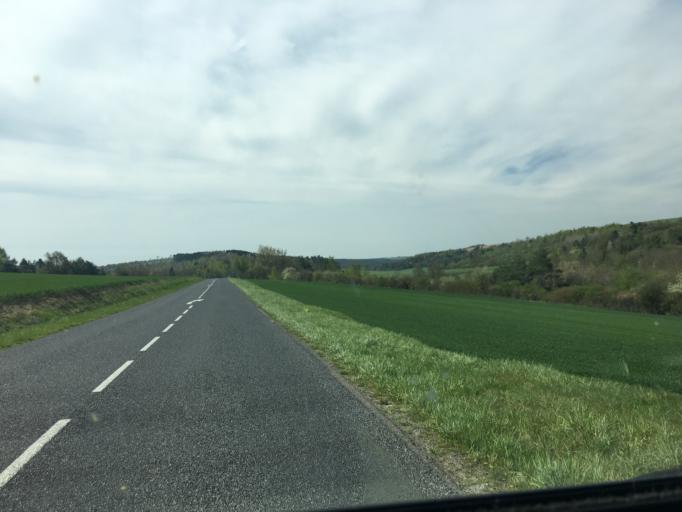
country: FR
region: Lorraine
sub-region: Departement de la Meuse
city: Saint-Mihiel
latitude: 48.8516
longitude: 5.5166
